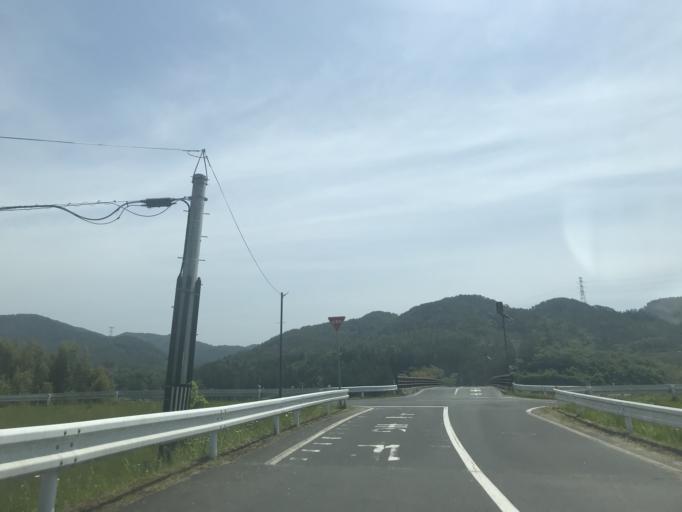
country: JP
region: Iwate
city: Ichinoseki
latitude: 38.9471
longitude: 141.2471
